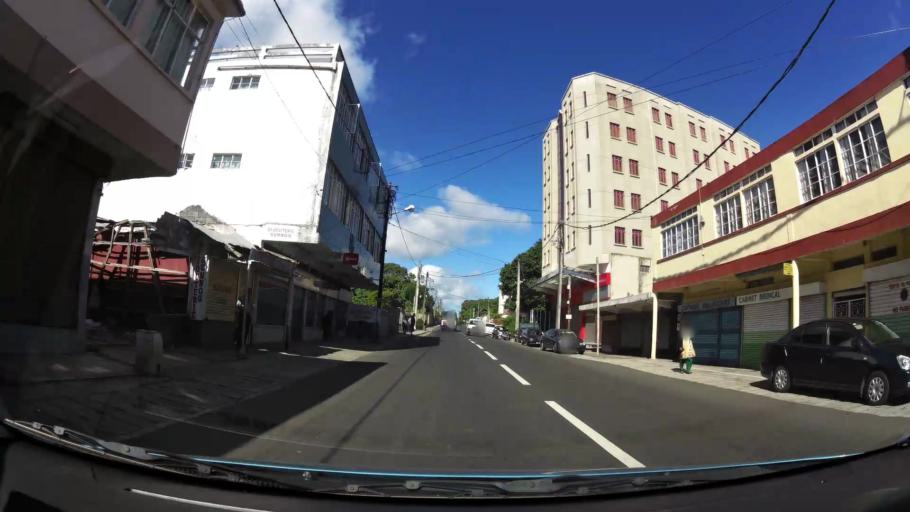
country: MU
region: Plaines Wilhems
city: Vacoas
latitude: -20.2997
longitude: 57.4927
